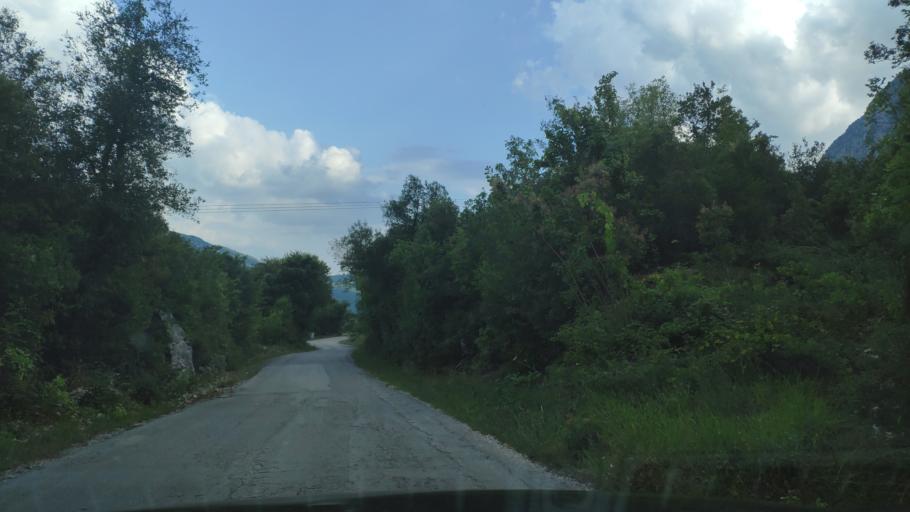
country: GR
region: Epirus
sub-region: Nomos Artas
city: Agios Dimitrios
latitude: 39.4467
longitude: 21.0165
